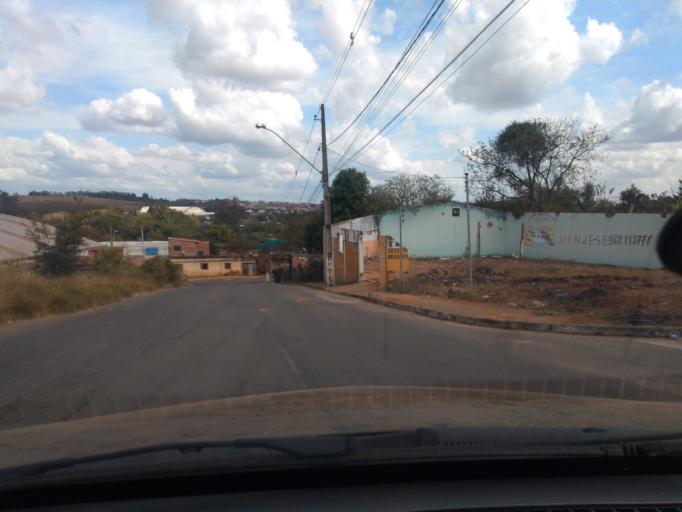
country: BR
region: Minas Gerais
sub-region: Tres Coracoes
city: Tres Coracoes
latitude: -21.6973
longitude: -45.2421
